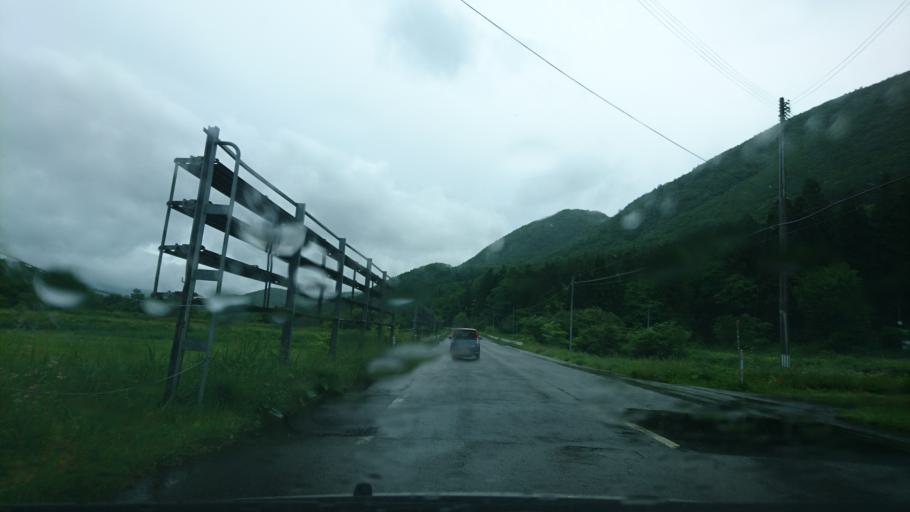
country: JP
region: Iwate
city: Ichinoseki
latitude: 39.0013
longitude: 140.8977
